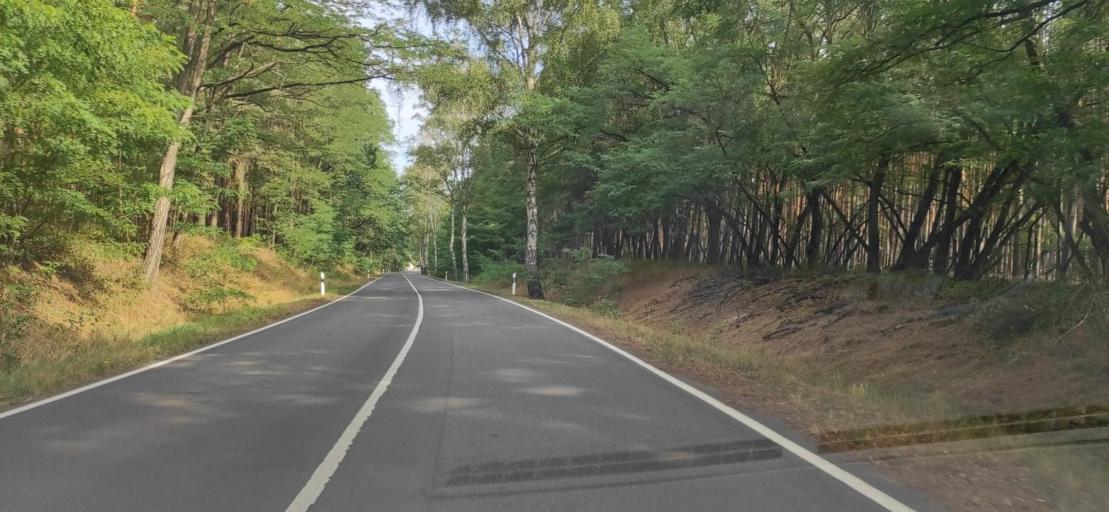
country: DE
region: Brandenburg
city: Forst
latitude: 51.6839
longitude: 14.7215
